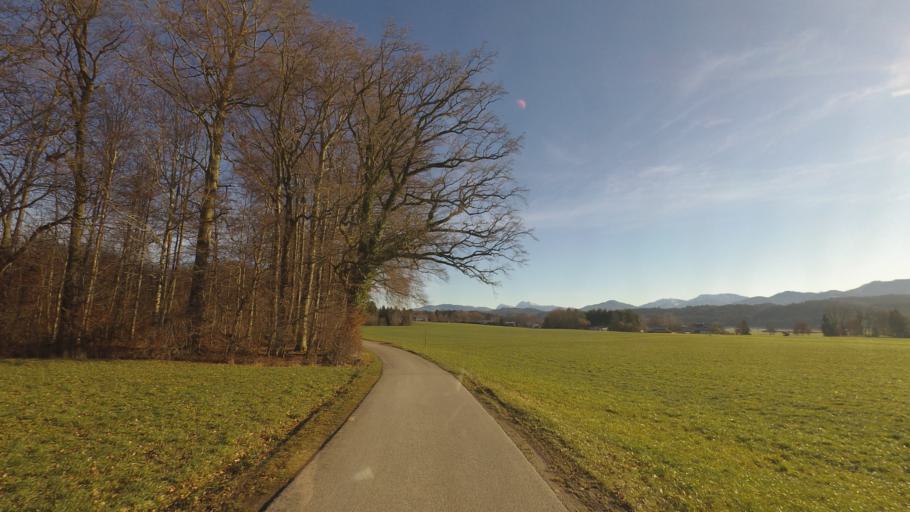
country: DE
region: Bavaria
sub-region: Upper Bavaria
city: Grabenstatt
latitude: 47.8545
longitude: 12.5506
